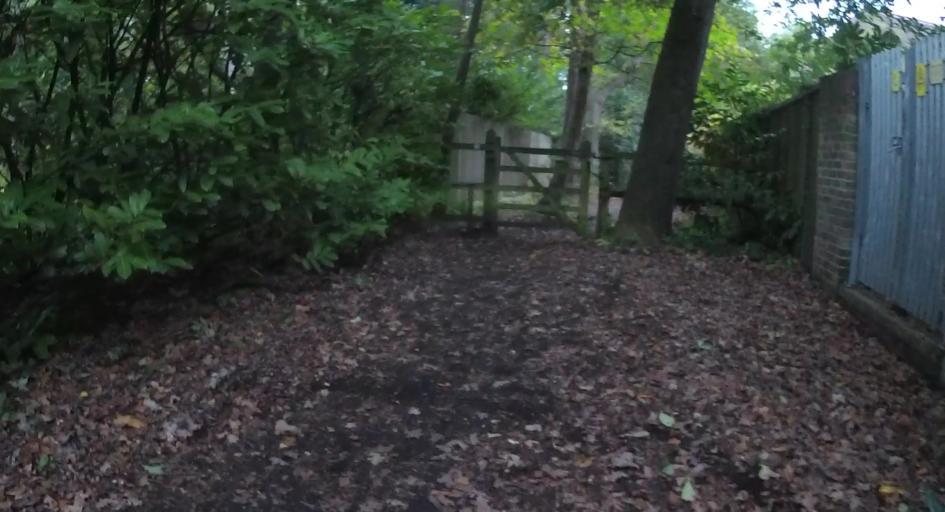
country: GB
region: England
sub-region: Bracknell Forest
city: Crowthorne
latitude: 51.3710
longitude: -0.8122
